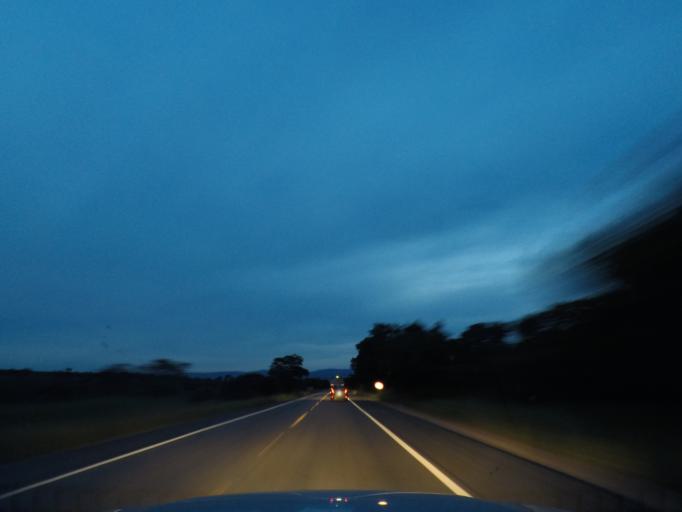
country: BR
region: Bahia
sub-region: Andarai
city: Vera Cruz
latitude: -12.4948
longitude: -41.3091
